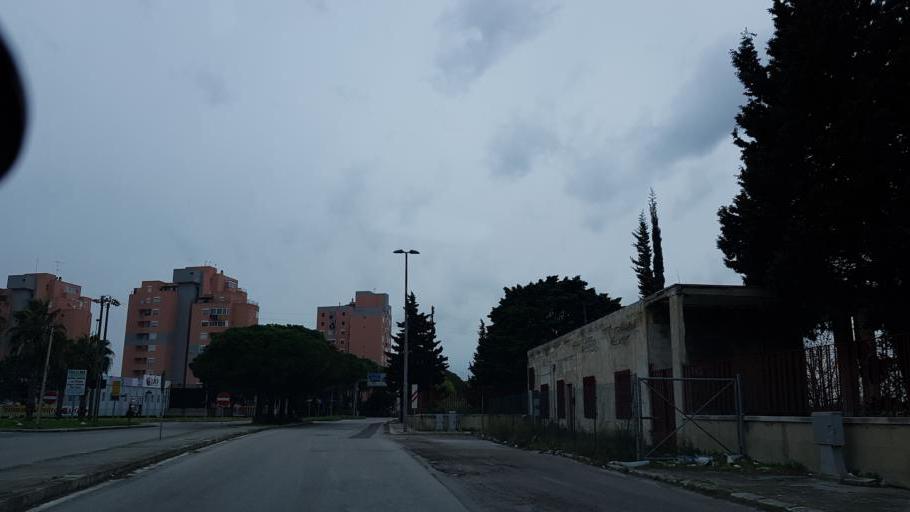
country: IT
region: Apulia
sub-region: Provincia di Brindisi
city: Brindisi
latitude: 40.6341
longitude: 17.9535
